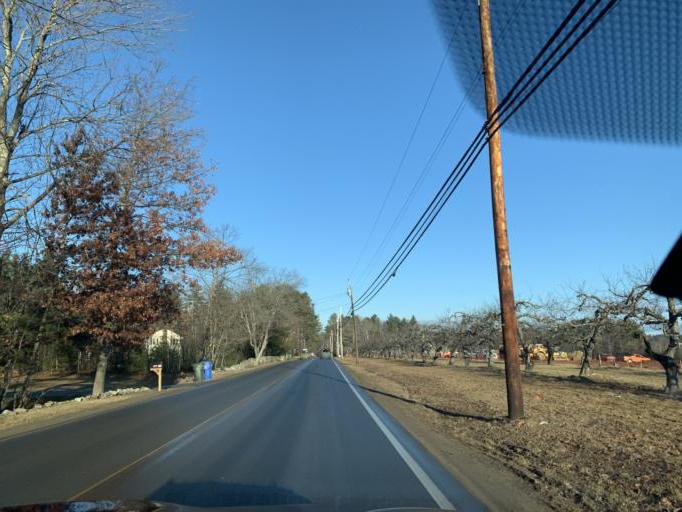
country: US
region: New Hampshire
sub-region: Rockingham County
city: Londonderry
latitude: 42.8686
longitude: -71.3544
